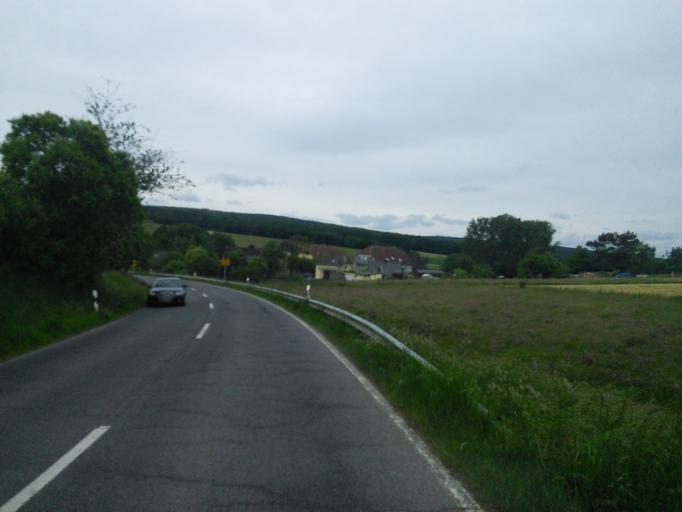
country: DE
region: North Rhine-Westphalia
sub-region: Regierungsbezirk Koln
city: Rheinbach
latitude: 50.5994
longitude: 6.8930
